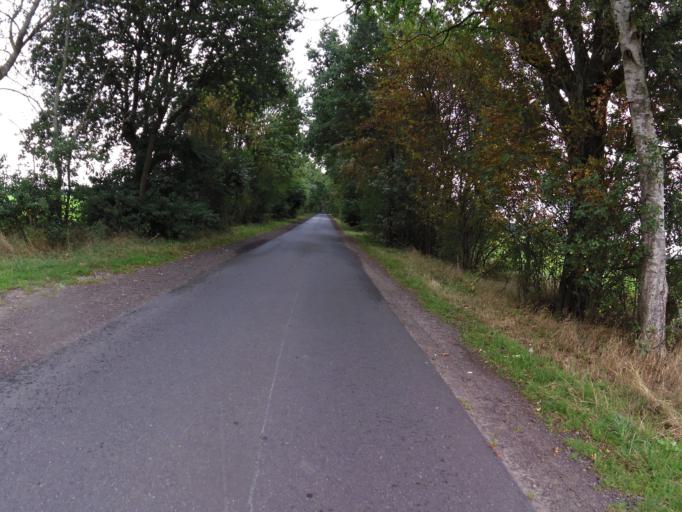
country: DE
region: Lower Saxony
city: Helvesiek
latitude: 53.2020
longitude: 9.4620
